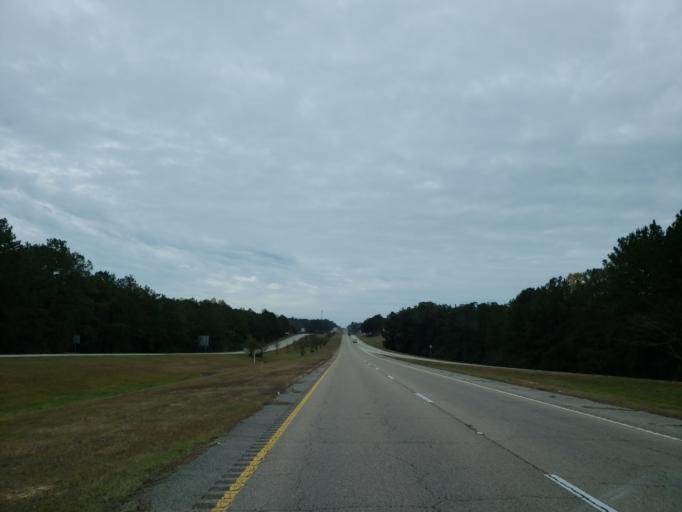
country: US
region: Mississippi
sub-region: Forrest County
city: Hattiesburg
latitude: 31.2416
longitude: -89.2747
